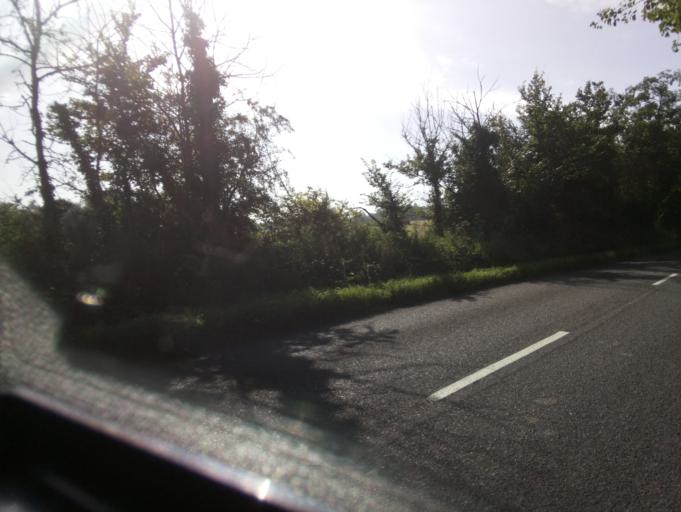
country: GB
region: England
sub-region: Oxfordshire
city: Faringdon
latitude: 51.6639
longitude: -1.5844
